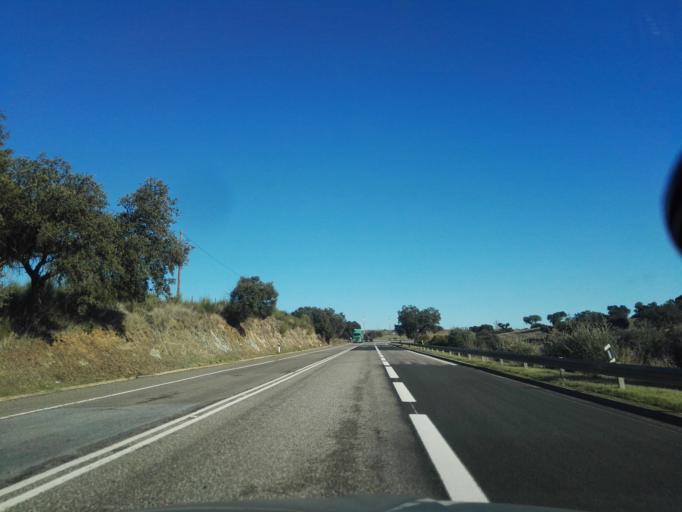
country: PT
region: Evora
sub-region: Vila Vicosa
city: Vila Vicosa
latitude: 38.8472
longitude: -7.3711
